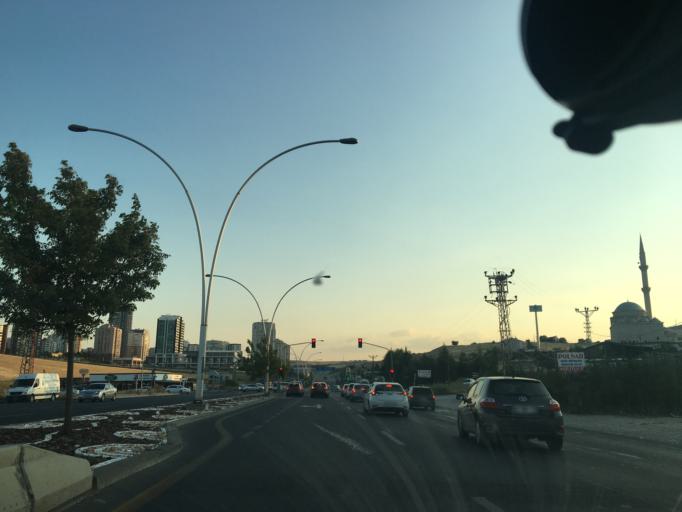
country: TR
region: Ankara
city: Etimesgut
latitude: 39.8719
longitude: 32.6448
